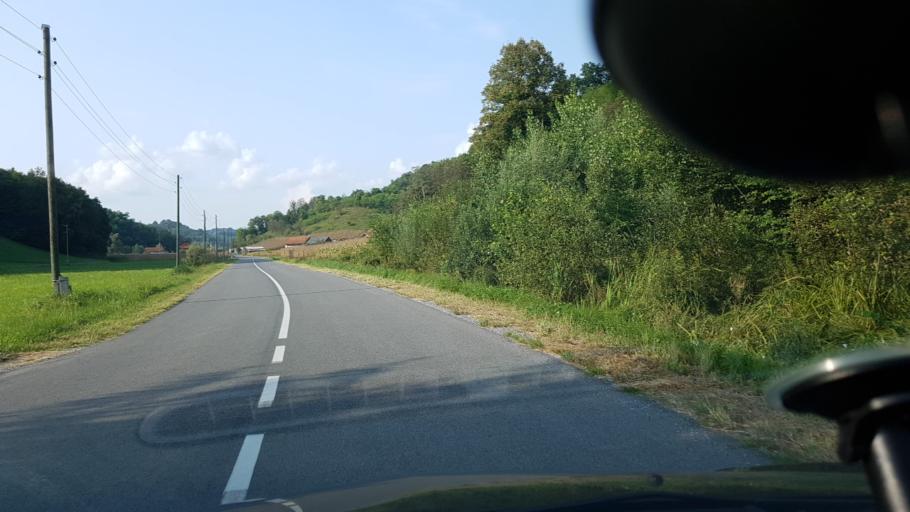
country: HR
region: Zagrebacka
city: Jakovlje
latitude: 46.0122
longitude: 15.7764
